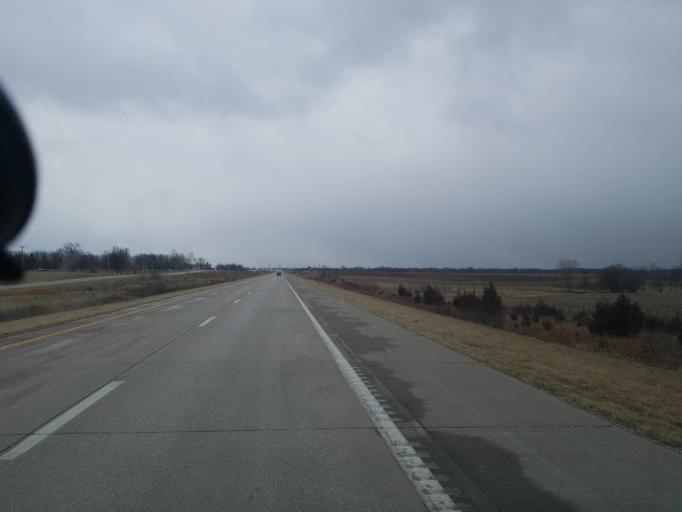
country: US
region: Missouri
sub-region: Randolph County
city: Moberly
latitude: 39.4817
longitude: -92.4345
